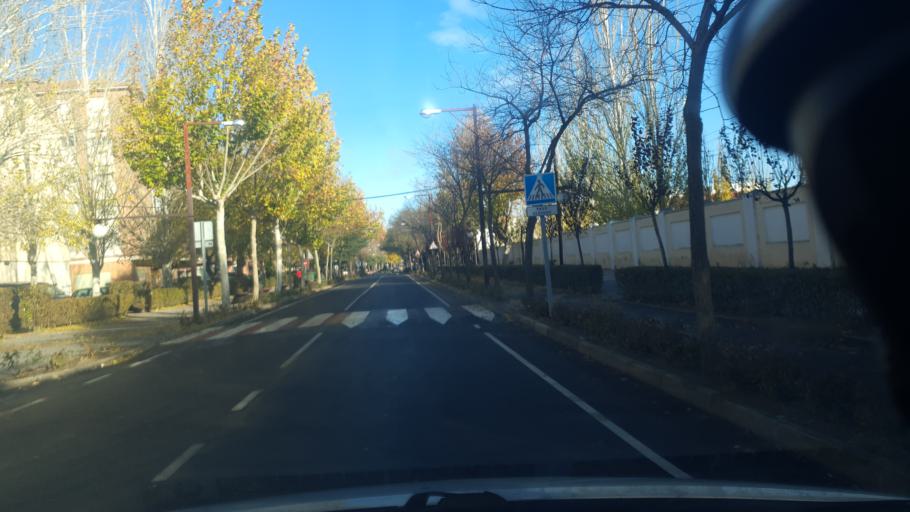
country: ES
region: Castille and Leon
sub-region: Provincia de Avila
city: Arevalo
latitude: 41.0552
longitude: -4.7205
